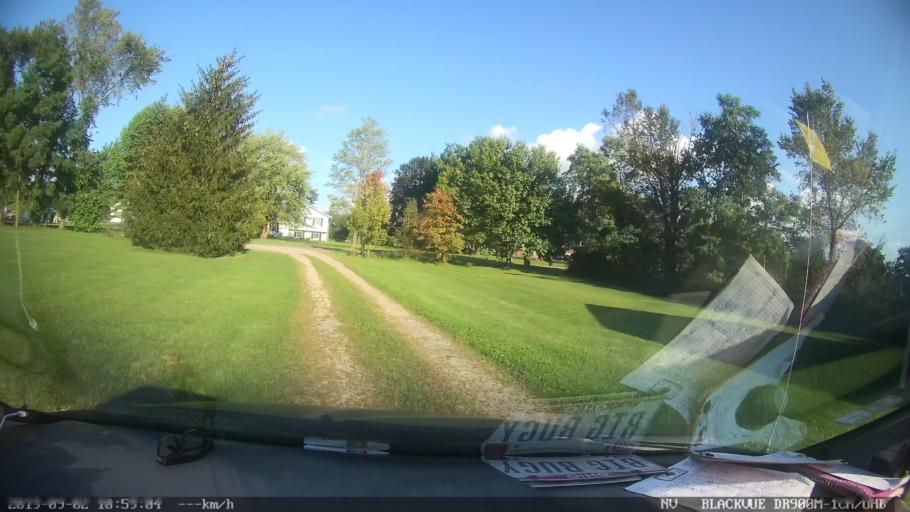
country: US
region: Ohio
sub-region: Morrow County
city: Cardington
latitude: 40.4458
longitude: -82.8748
